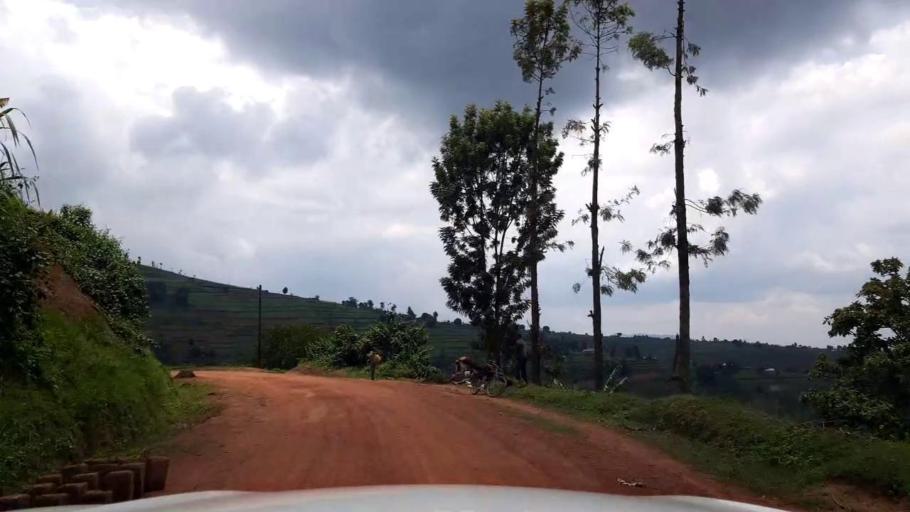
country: RW
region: Northern Province
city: Byumba
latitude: -1.4788
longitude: 29.9021
